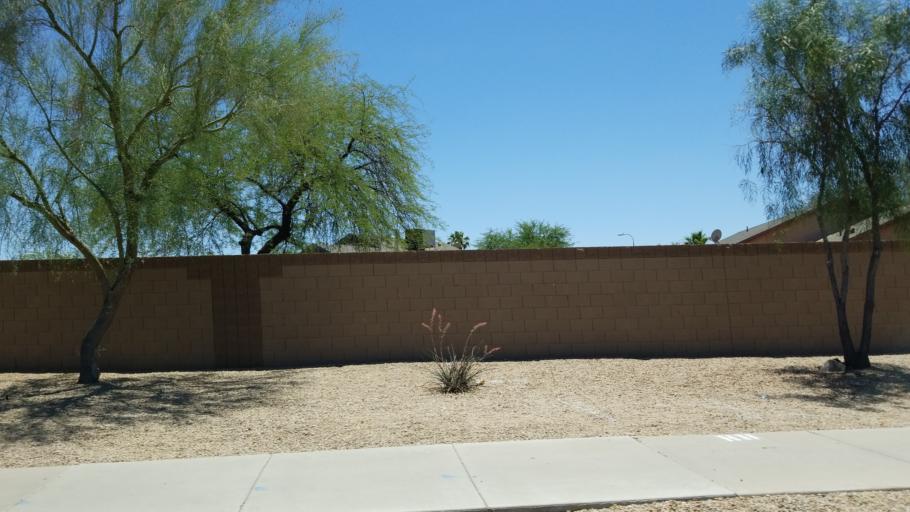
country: US
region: Arizona
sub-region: Maricopa County
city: Tolleson
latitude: 33.5087
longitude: -112.2426
